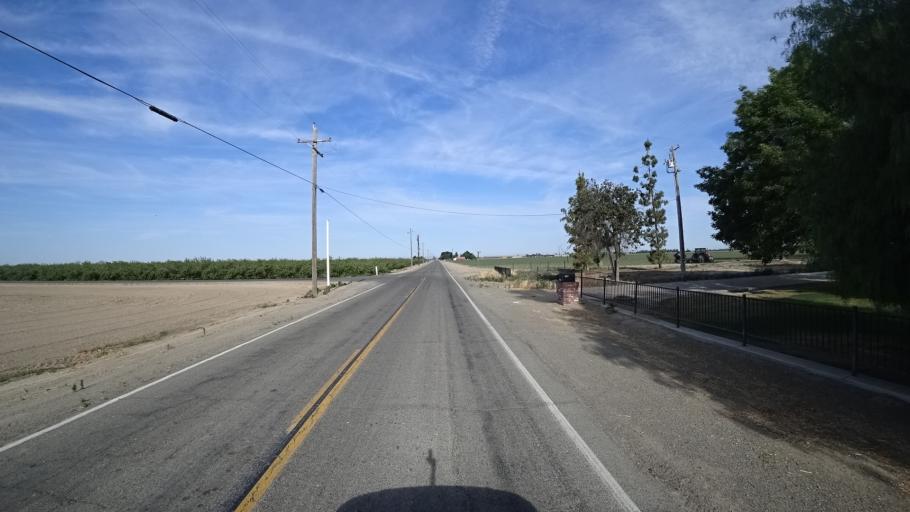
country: US
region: California
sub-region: Fresno County
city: Kingsburg
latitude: 36.4014
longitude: -119.5463
